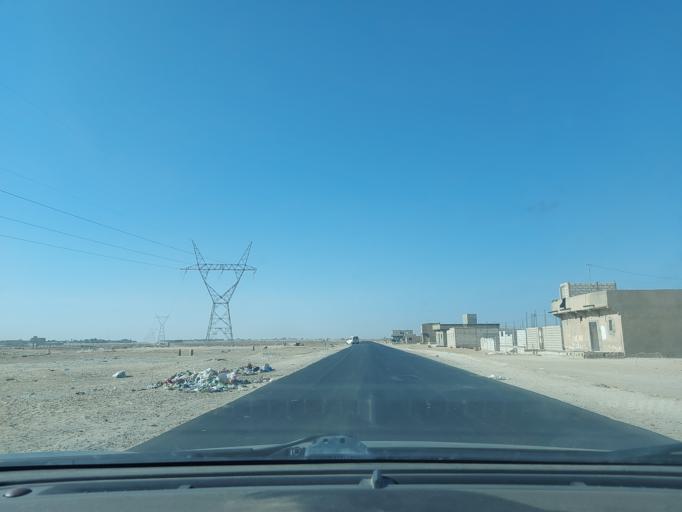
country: MR
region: Nouakchott
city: Nouakchott
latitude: 18.0103
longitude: -15.9875
